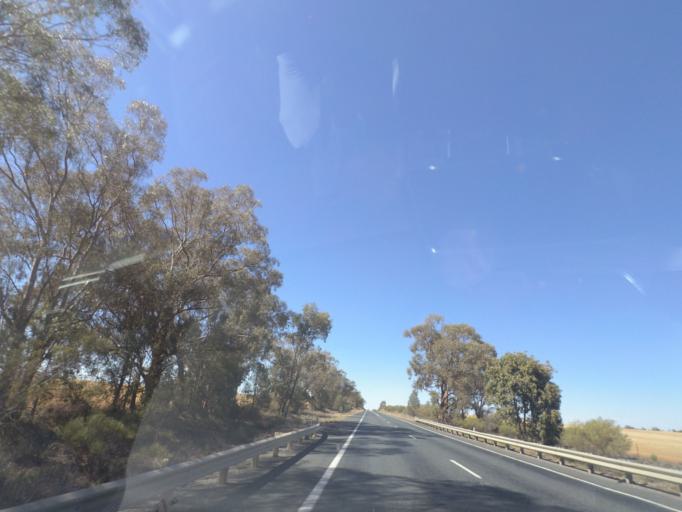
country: AU
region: New South Wales
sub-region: Bland
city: West Wyalong
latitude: -34.1769
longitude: 147.1141
